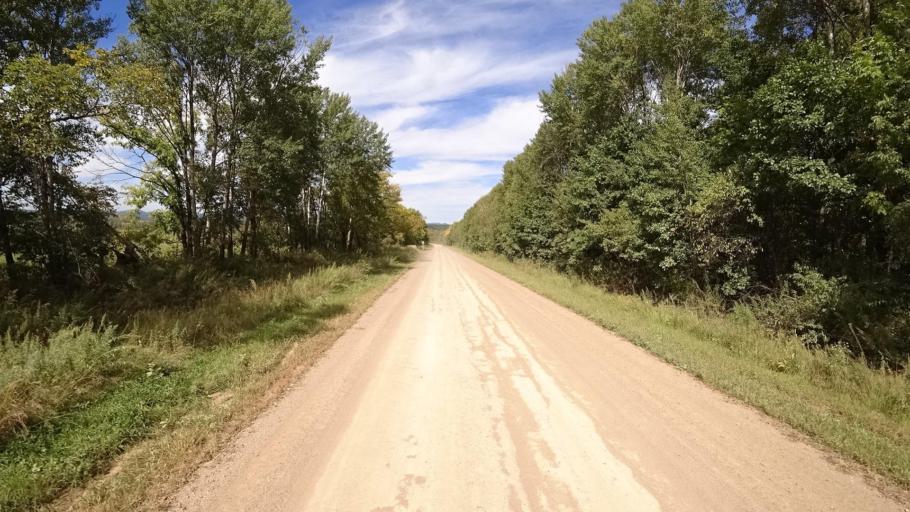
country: RU
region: Primorskiy
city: Yakovlevka
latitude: 44.6300
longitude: 133.6014
